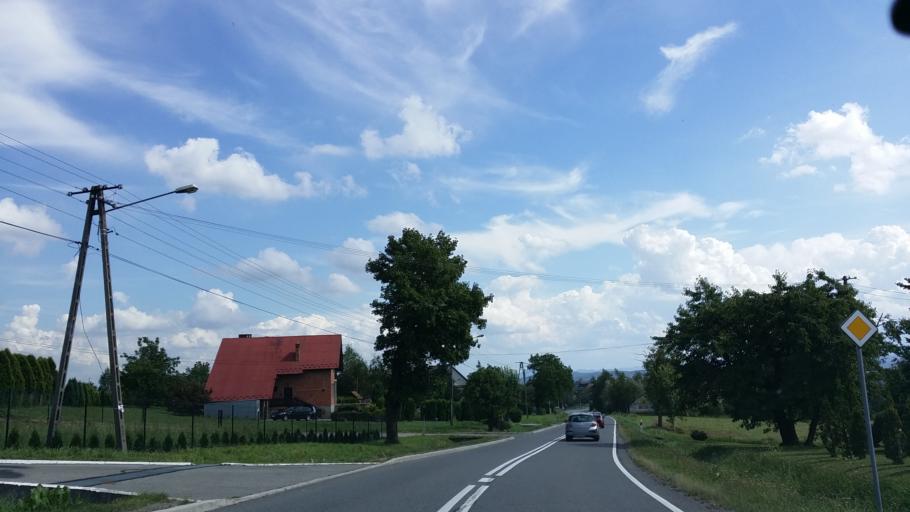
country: PL
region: Lesser Poland Voivodeship
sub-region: Powiat wielicki
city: Pawlikowice
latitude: 49.9246
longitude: 20.0765
